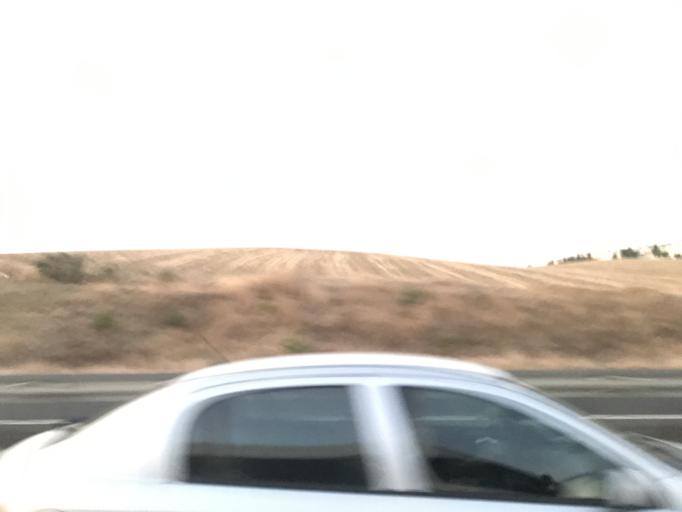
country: TR
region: Tekirdag
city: Corlu
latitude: 41.0039
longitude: 27.6966
